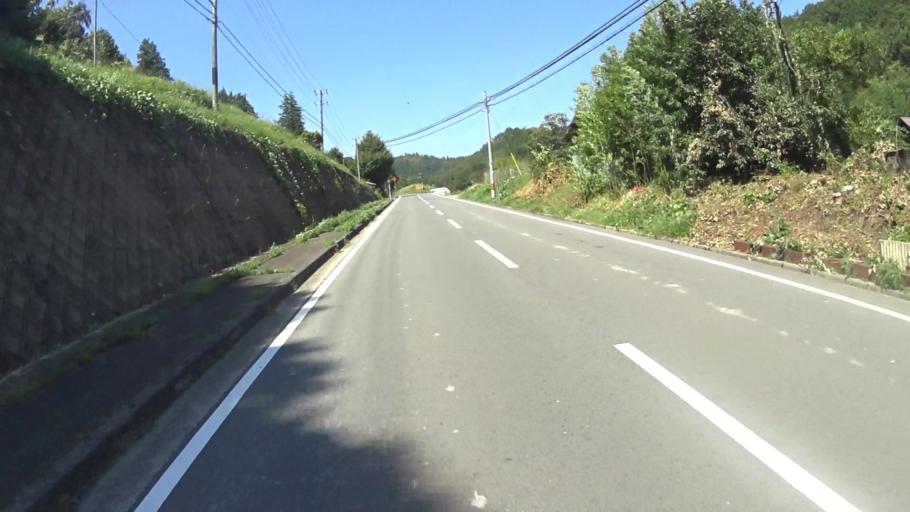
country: JP
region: Kyoto
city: Kameoka
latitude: 34.9395
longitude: 135.5370
